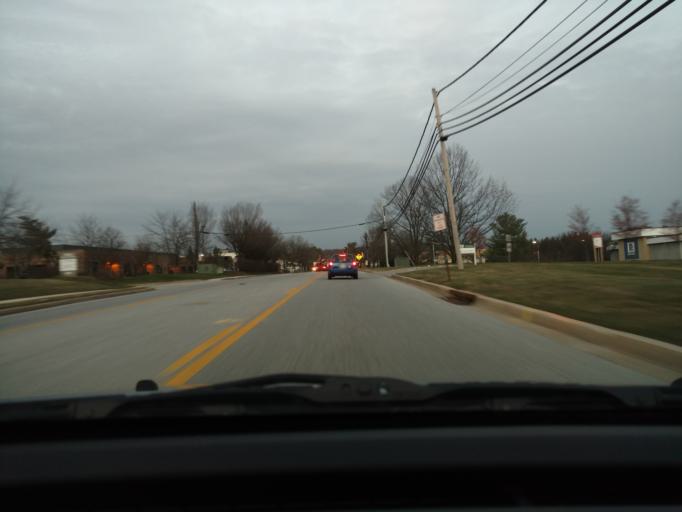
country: US
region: Maryland
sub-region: Baltimore County
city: Cockeysville
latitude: 39.4811
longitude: -76.6586
